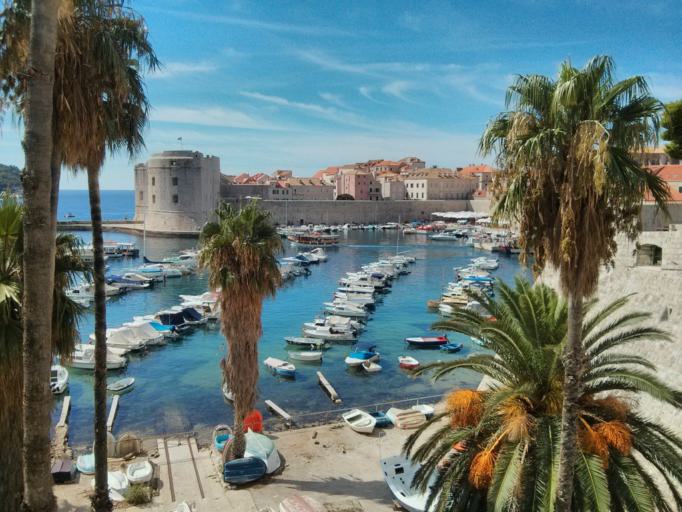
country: HR
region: Dubrovacko-Neretvanska
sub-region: Grad Dubrovnik
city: Dubrovnik
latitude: 42.6420
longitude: 18.1128
